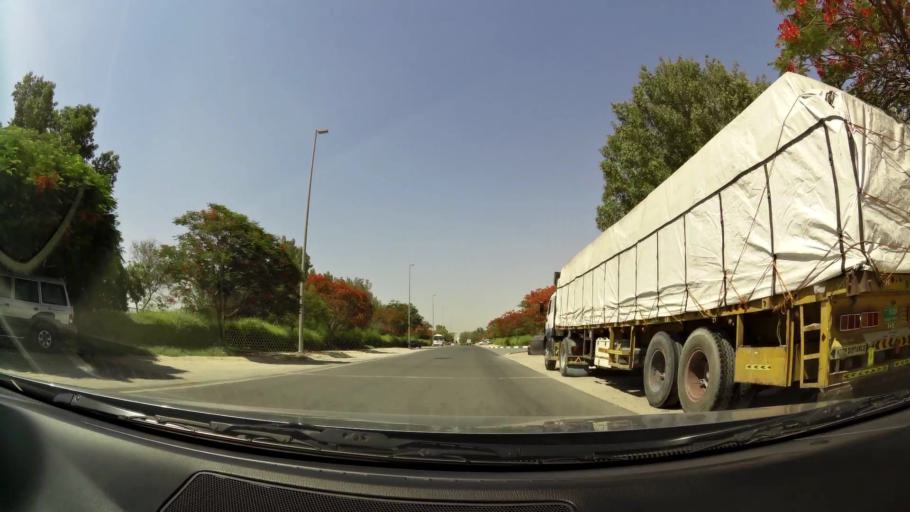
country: AE
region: Dubai
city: Dubai
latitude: 24.9797
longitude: 55.1469
